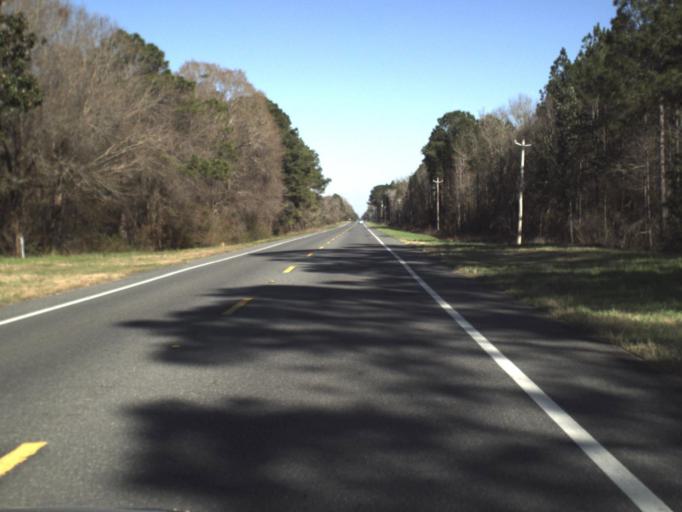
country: US
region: Florida
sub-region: Washington County
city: Chipley
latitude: 30.7864
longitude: -85.4476
